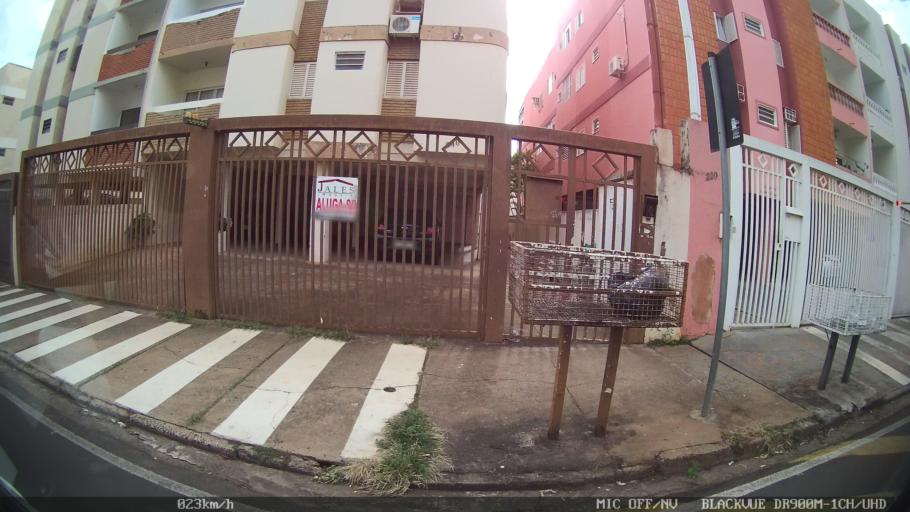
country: BR
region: Sao Paulo
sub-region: Sao Jose Do Rio Preto
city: Sao Jose do Rio Preto
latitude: -20.8287
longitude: -49.3988
